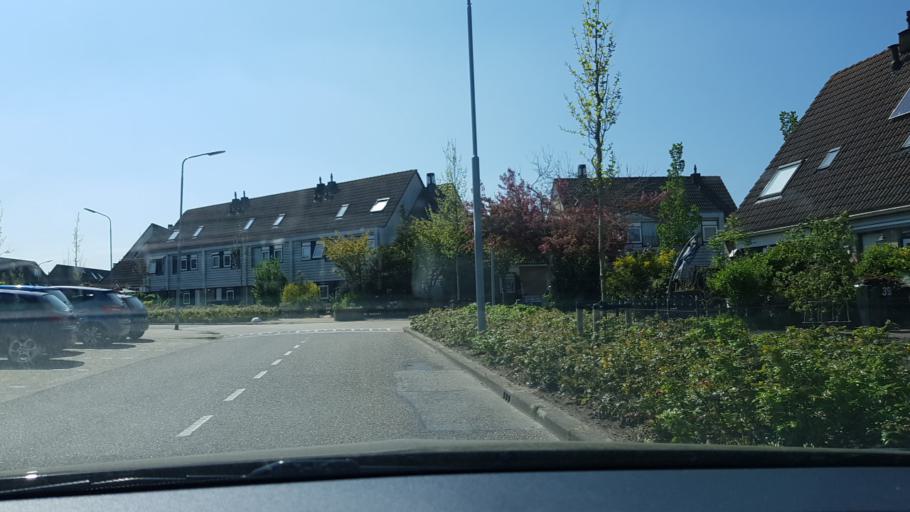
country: NL
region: North Holland
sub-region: Gemeente Haarlemmermeer
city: Hoofddorp
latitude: 52.3176
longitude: 4.6631
